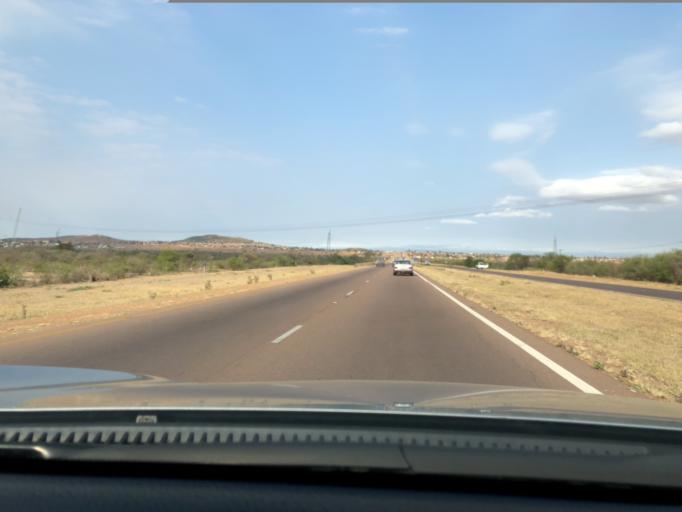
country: ZA
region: Limpopo
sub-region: Capricorn District Municipality
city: Polokwane
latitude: -23.8954
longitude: 29.6321
